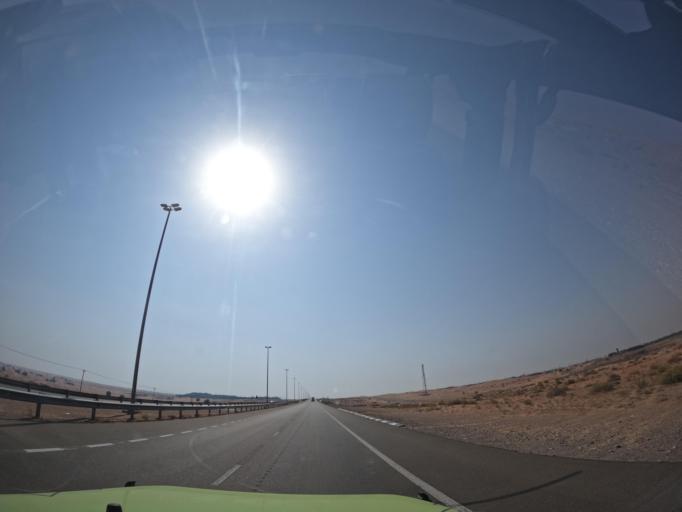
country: OM
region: Al Buraimi
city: Al Buraymi
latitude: 24.4231
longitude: 55.6866
